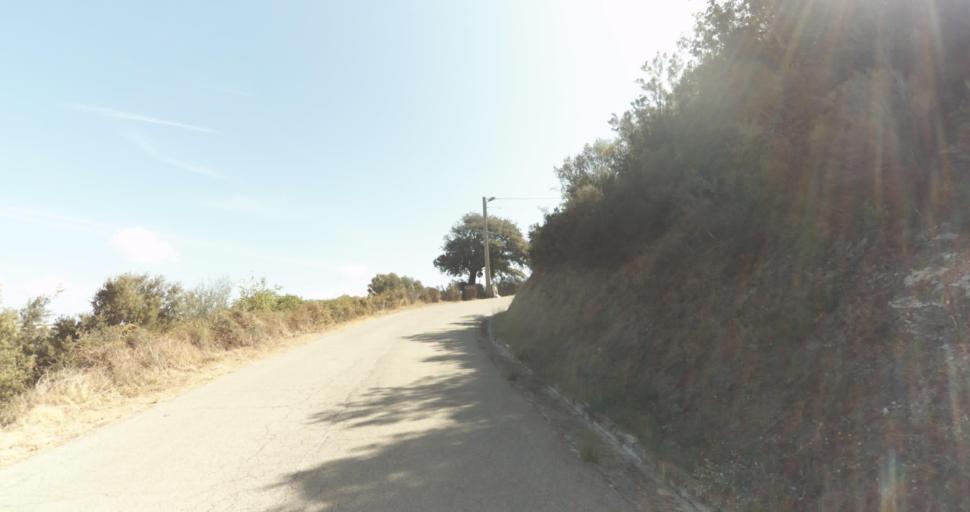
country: FR
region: Corsica
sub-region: Departement de la Corse-du-Sud
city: Ajaccio
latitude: 41.9279
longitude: 8.7060
